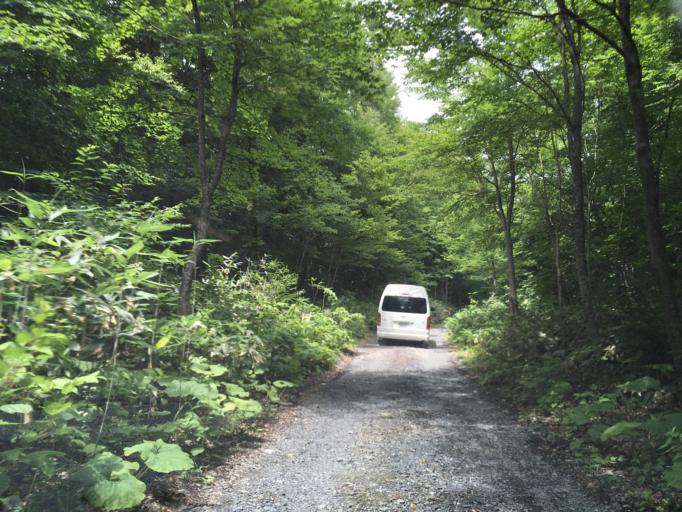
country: JP
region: Iwate
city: Ichinoseki
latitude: 38.9498
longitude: 140.8566
